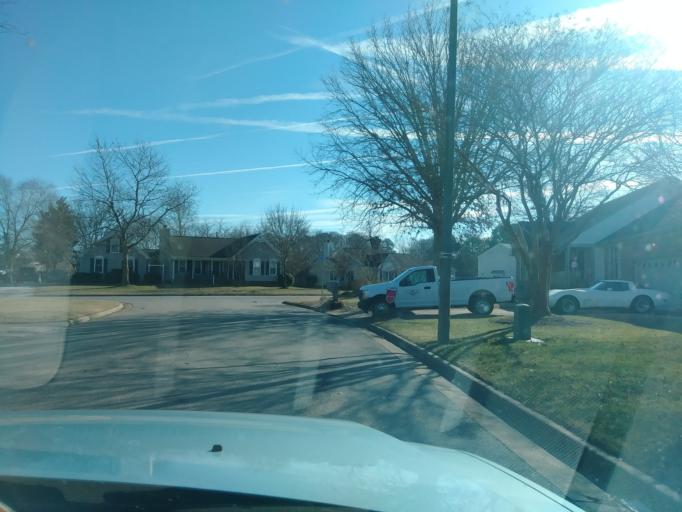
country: US
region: Virginia
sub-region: City of Chesapeake
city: Chesapeake
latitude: 36.7546
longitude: -76.2096
